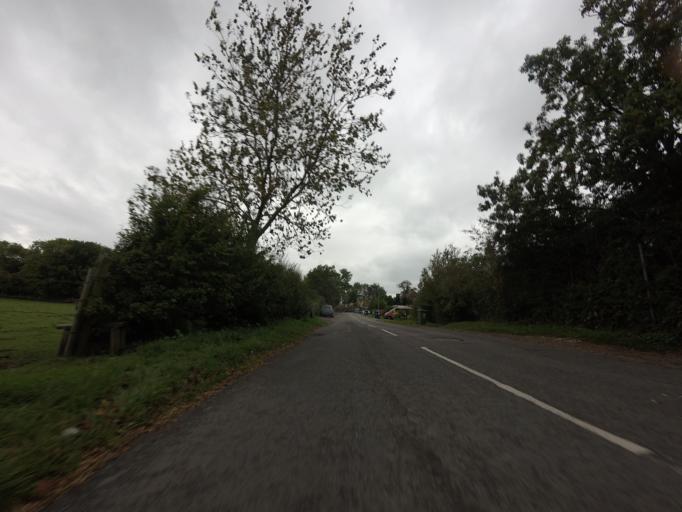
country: GB
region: England
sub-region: Cambridgeshire
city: Haslingfield
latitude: 52.1536
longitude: 0.0345
